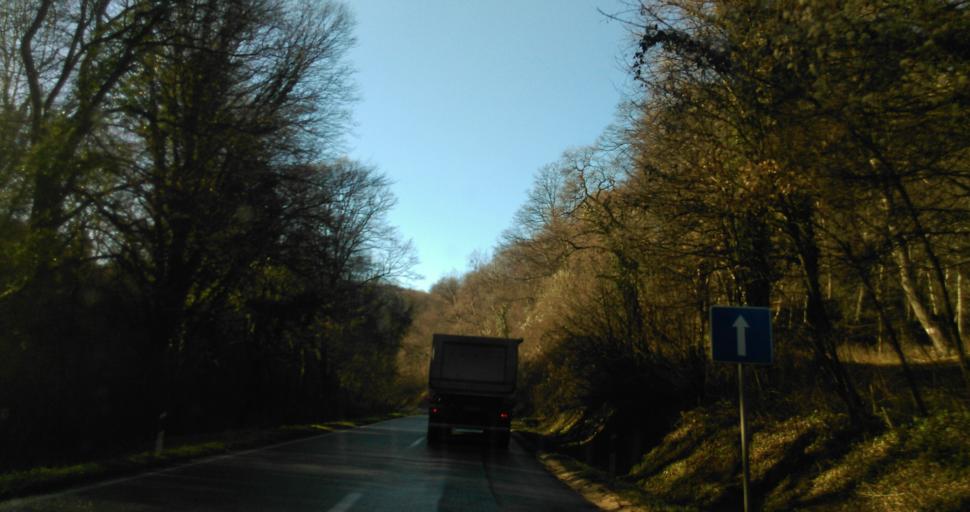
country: RS
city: Vrdnik
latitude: 45.1751
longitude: 19.8330
